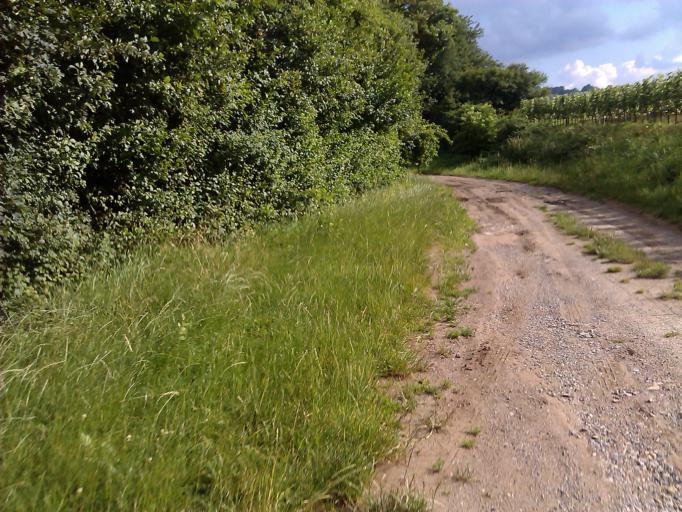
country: DE
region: Baden-Wuerttemberg
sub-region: Regierungsbezirk Stuttgart
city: Lauffen am Neckar
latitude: 49.0619
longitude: 9.1502
